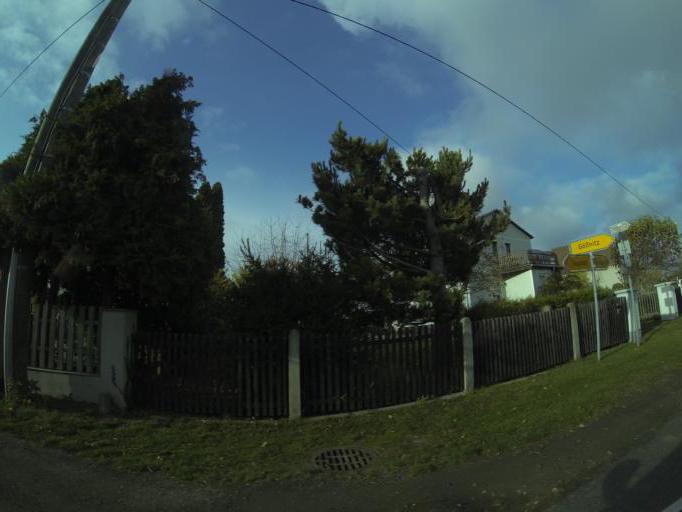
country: DE
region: Thuringia
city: Gossnitz
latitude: 50.8996
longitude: 12.4141
